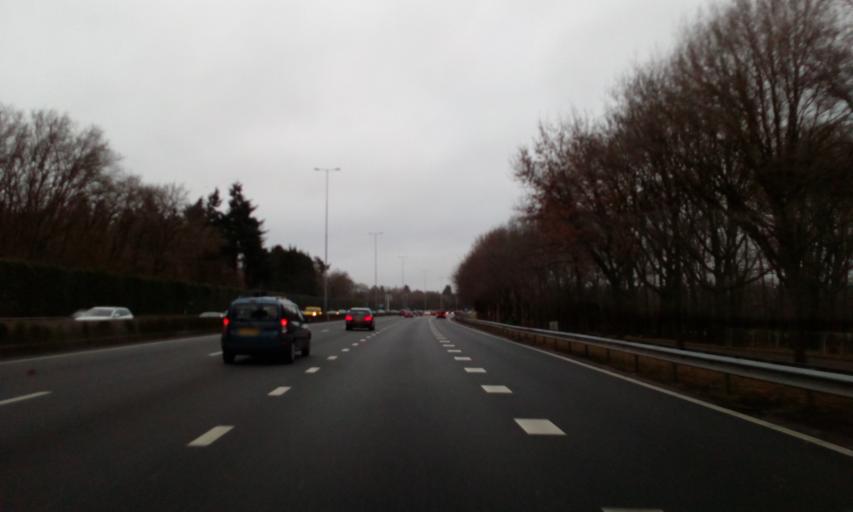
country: NL
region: North Holland
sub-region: Gemeente Laren
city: Laren
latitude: 52.2465
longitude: 5.2159
